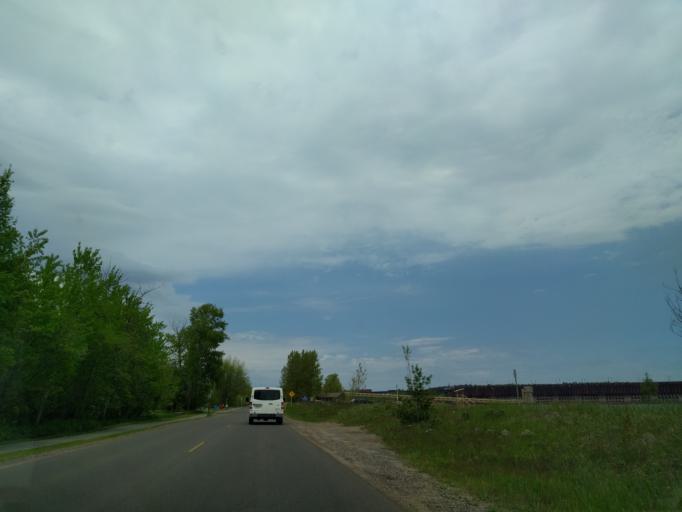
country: US
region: Michigan
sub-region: Marquette County
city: Marquette
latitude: 46.5732
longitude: -87.3935
